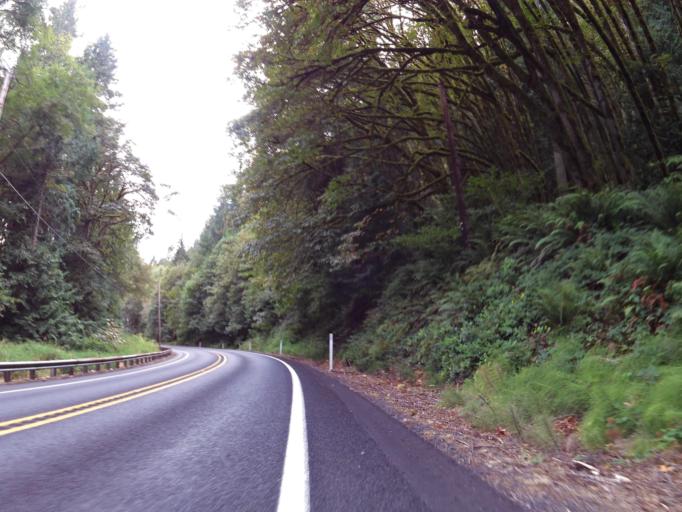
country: US
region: Oregon
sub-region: Columbia County
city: Clatskanie
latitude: 46.1728
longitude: -123.2324
